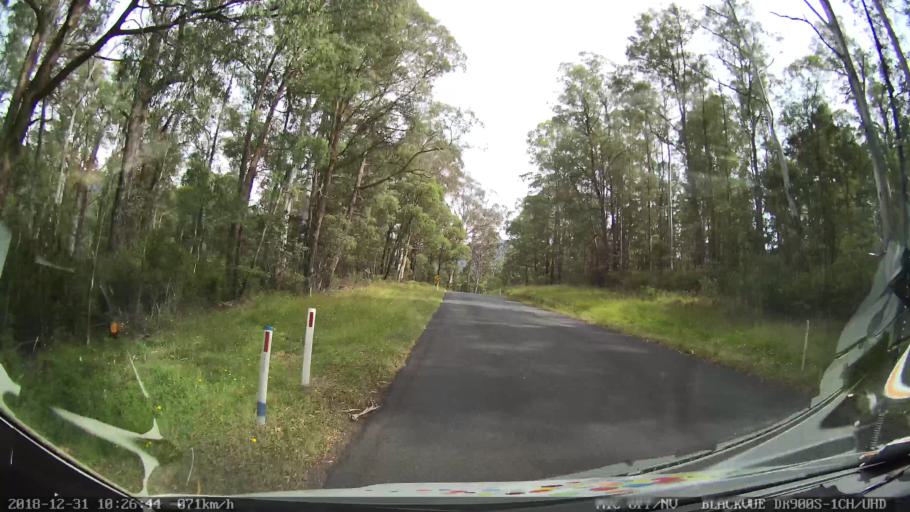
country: AU
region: New South Wales
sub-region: Snowy River
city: Jindabyne
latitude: -36.4922
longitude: 148.1406
